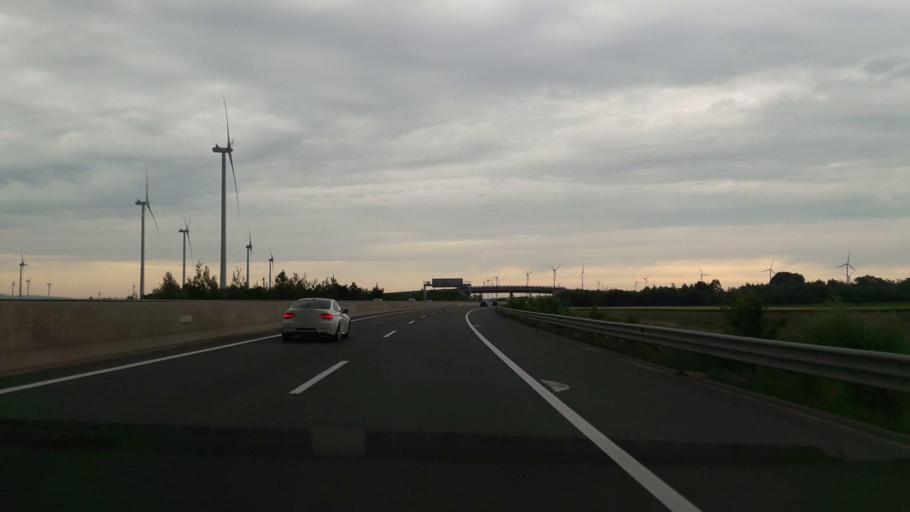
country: AT
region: Burgenland
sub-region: Politischer Bezirk Neusiedl am See
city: Parndorf
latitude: 48.0267
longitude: 16.8518
